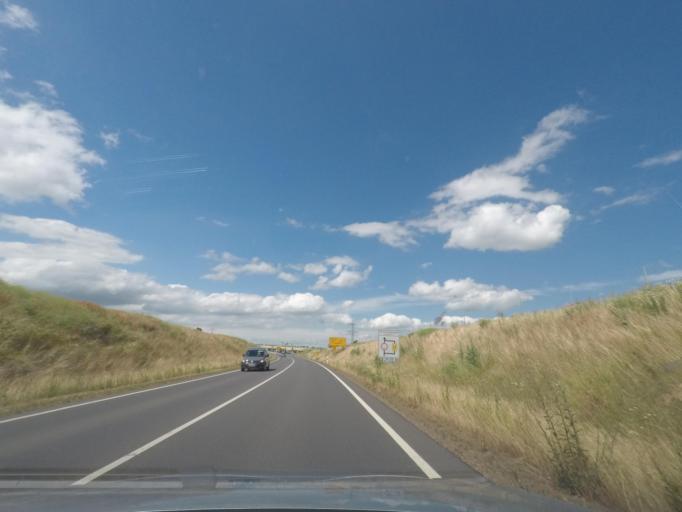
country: DE
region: Saxony-Anhalt
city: Gross Quenstedt
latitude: 51.9087
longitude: 11.1118
